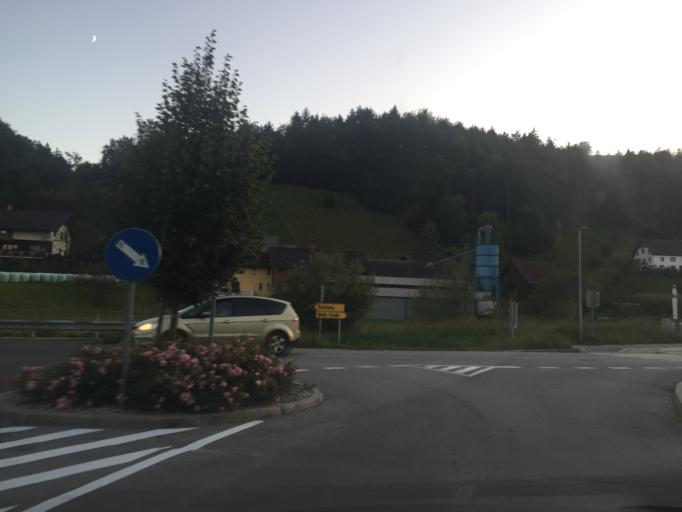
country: SI
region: Sostanj
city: Topolsica
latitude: 46.3826
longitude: 15.0294
